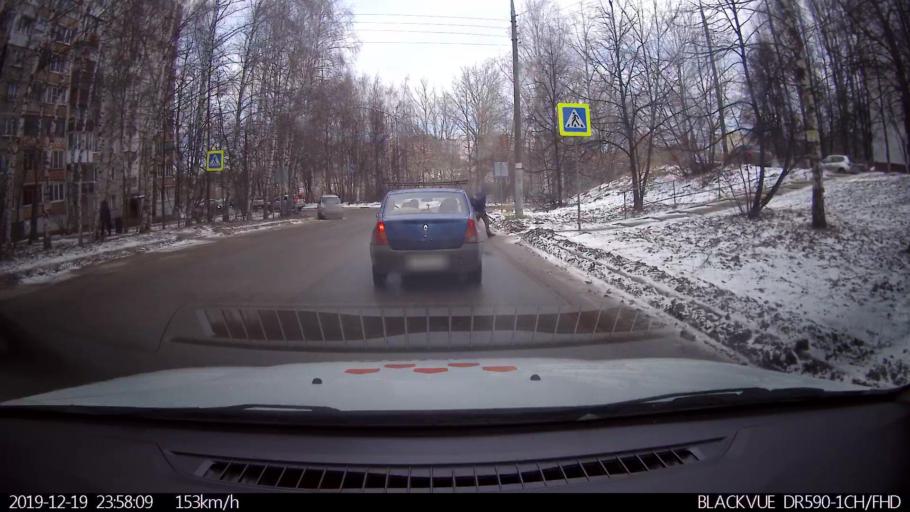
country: RU
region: Jaroslavl
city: Kukoboy
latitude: 58.8665
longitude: 39.6382
